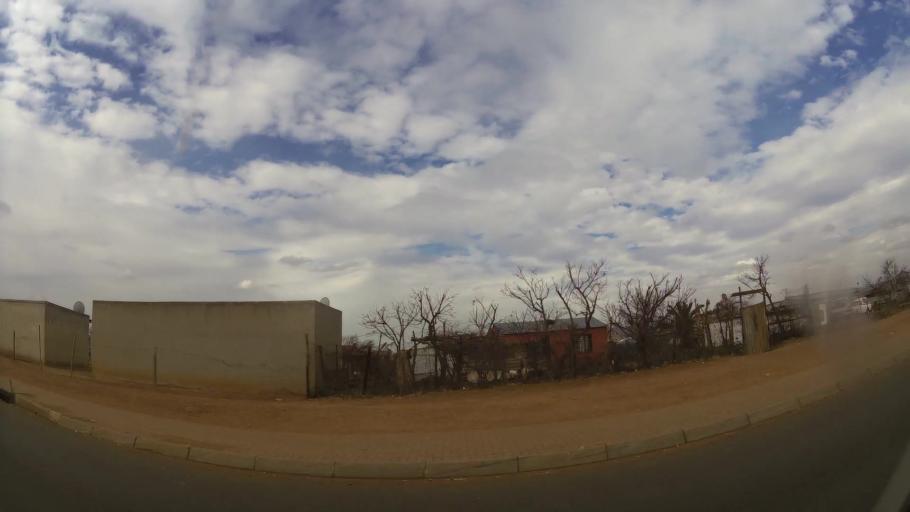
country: ZA
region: Gauteng
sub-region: Ekurhuleni Metropolitan Municipality
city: Germiston
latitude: -26.3985
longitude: 28.1569
